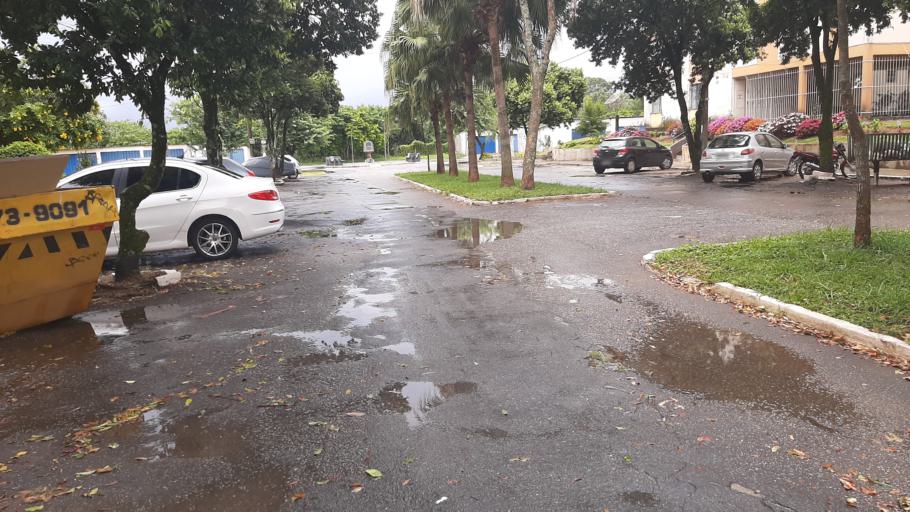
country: BR
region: Minas Gerais
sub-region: Sao Joao Del Rei
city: Sao Joao del Rei
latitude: -21.1257
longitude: -44.2355
